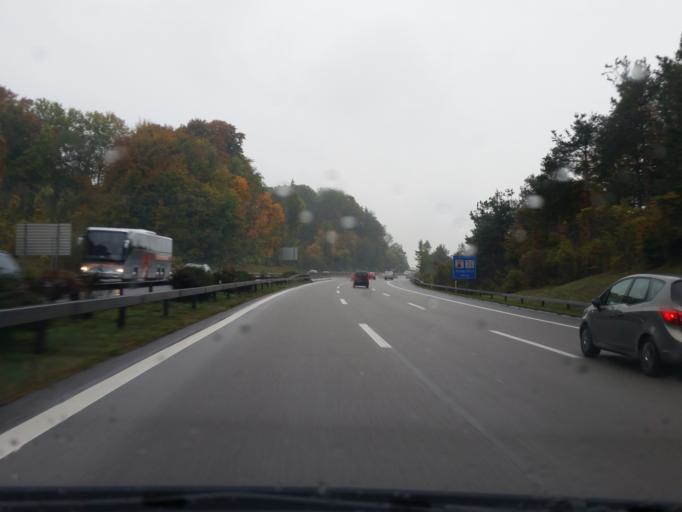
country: CH
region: Zurich
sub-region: Bezirk Winterthur
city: Toss
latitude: 47.4594
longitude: 8.7090
